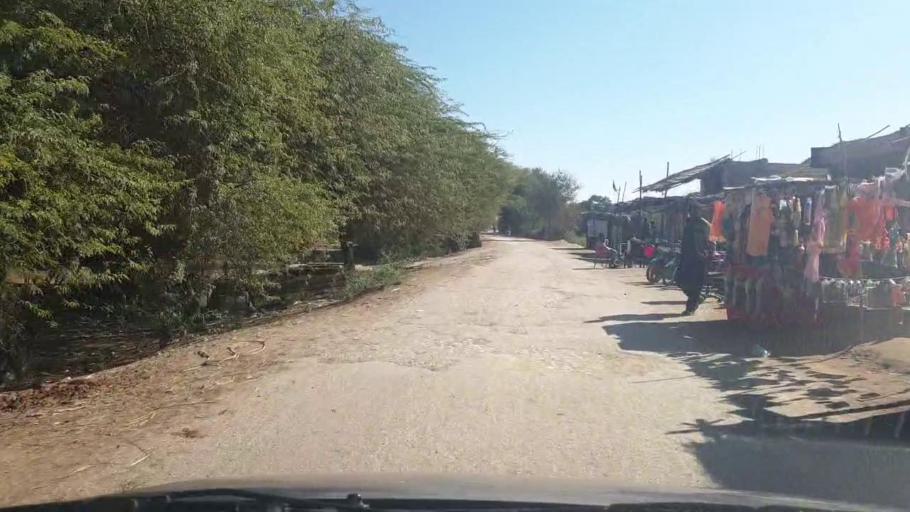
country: PK
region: Sindh
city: Bozdar
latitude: 27.0658
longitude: 68.6182
